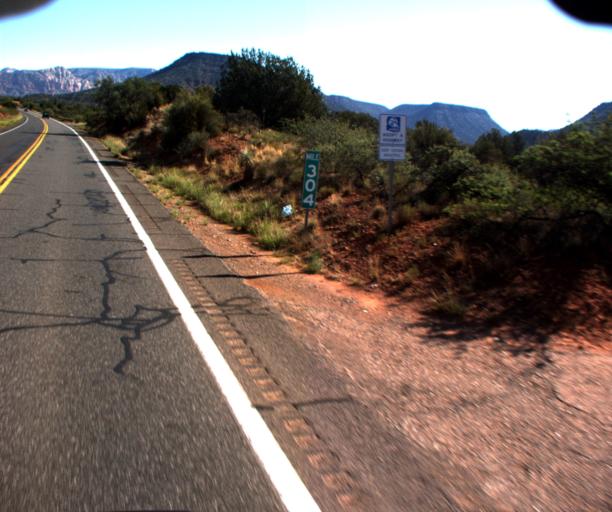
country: US
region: Arizona
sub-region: Yavapai County
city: Big Park
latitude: 34.7457
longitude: -111.7676
